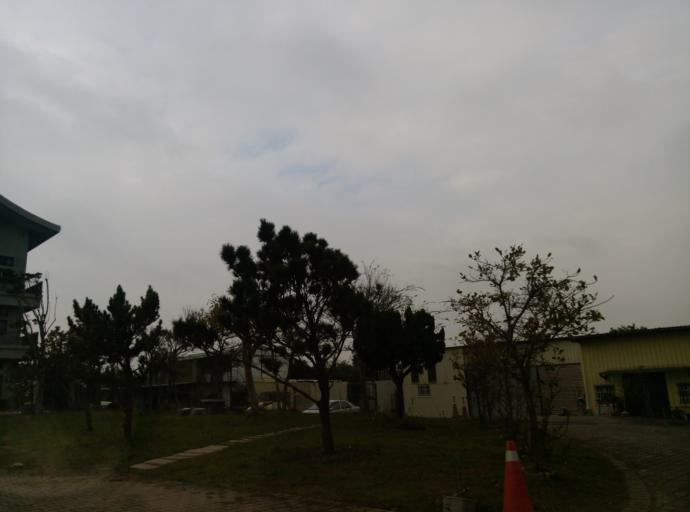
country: TW
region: Taiwan
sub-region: Hsinchu
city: Hsinchu
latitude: 24.7854
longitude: 120.9197
